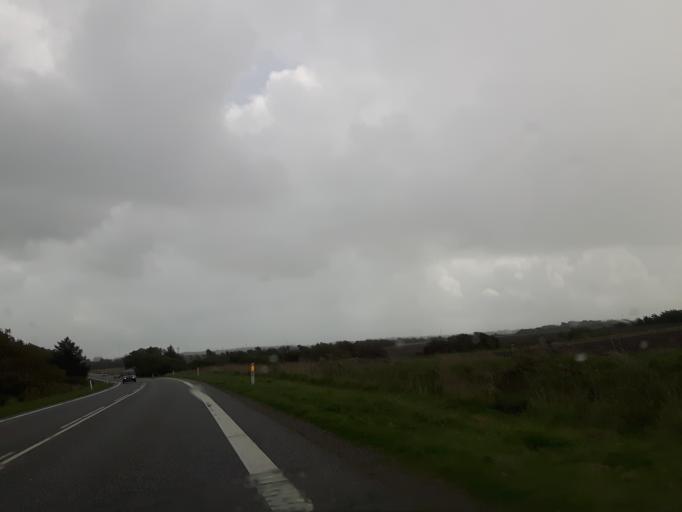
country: DK
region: North Denmark
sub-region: Thisted Kommune
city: Hurup
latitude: 56.6461
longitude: 8.4824
